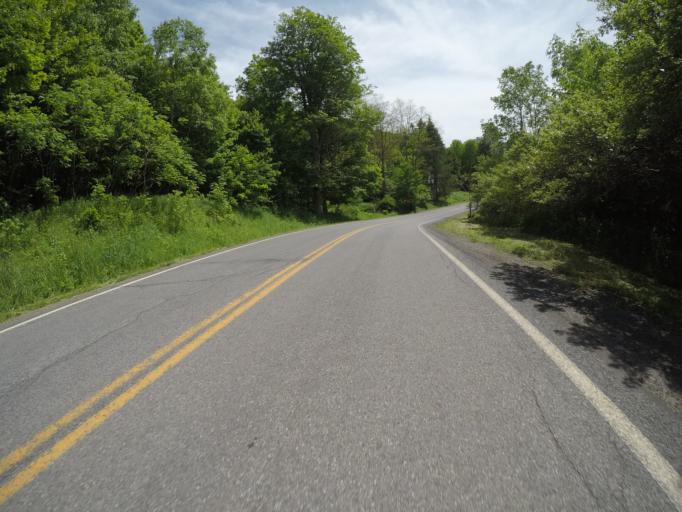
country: US
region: New York
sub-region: Delaware County
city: Delhi
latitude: 42.1389
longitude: -74.7997
